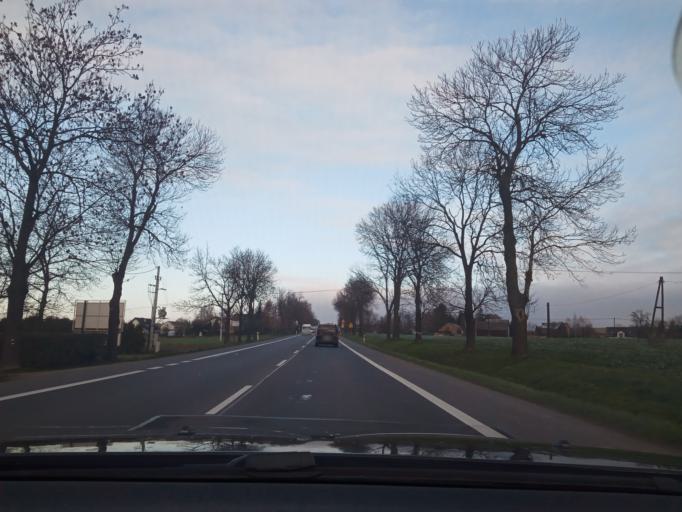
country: PL
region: Lesser Poland Voivodeship
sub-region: Powiat krakowski
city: Slomniki
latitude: 50.2622
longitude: 20.0786
